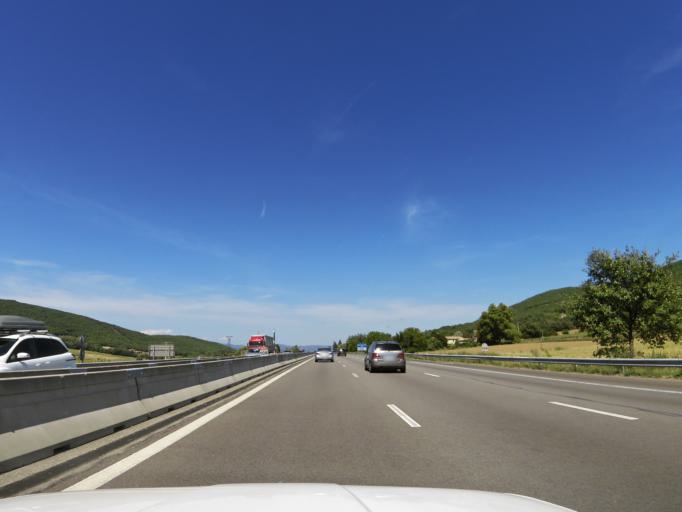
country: FR
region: Rhone-Alpes
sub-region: Departement de la Drome
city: Savasse
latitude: 44.6187
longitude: 4.7929
